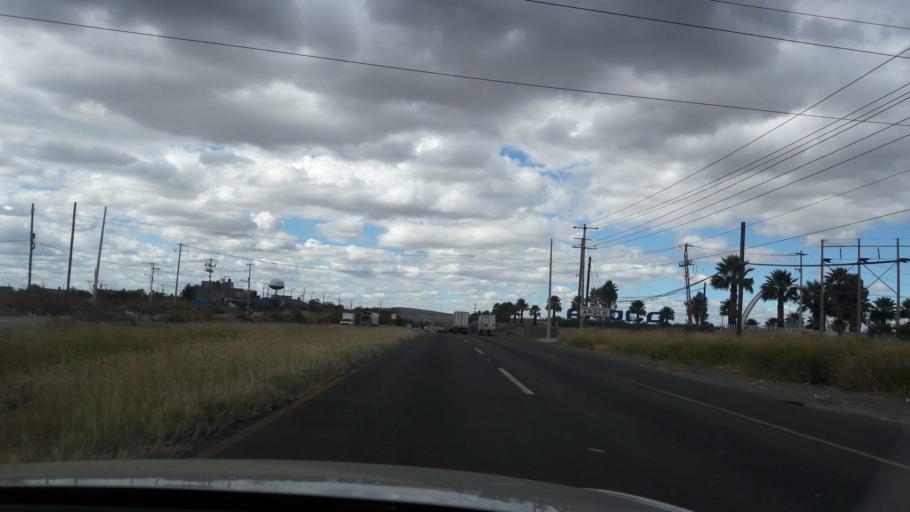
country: MX
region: Guanajuato
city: San Jose Temascatio
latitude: 20.6877
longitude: -101.3074
